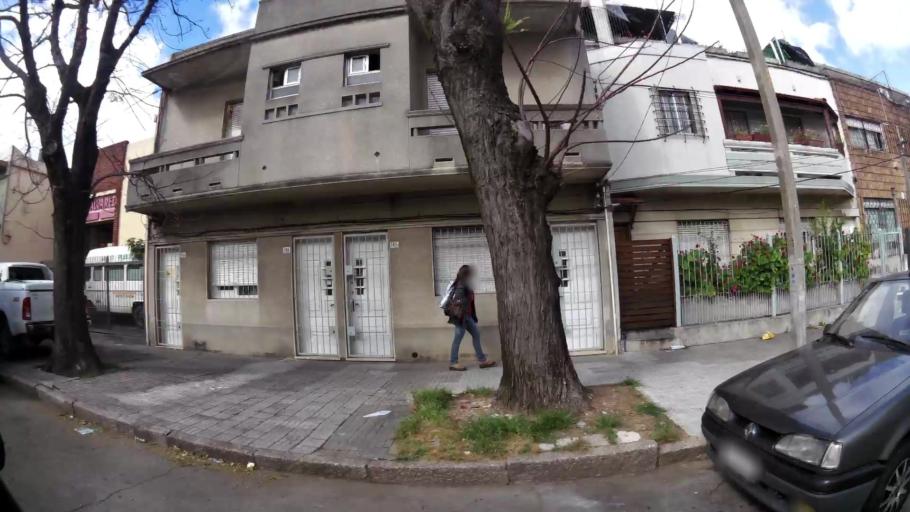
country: UY
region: Montevideo
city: Montevideo
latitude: -34.8834
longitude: -56.1656
